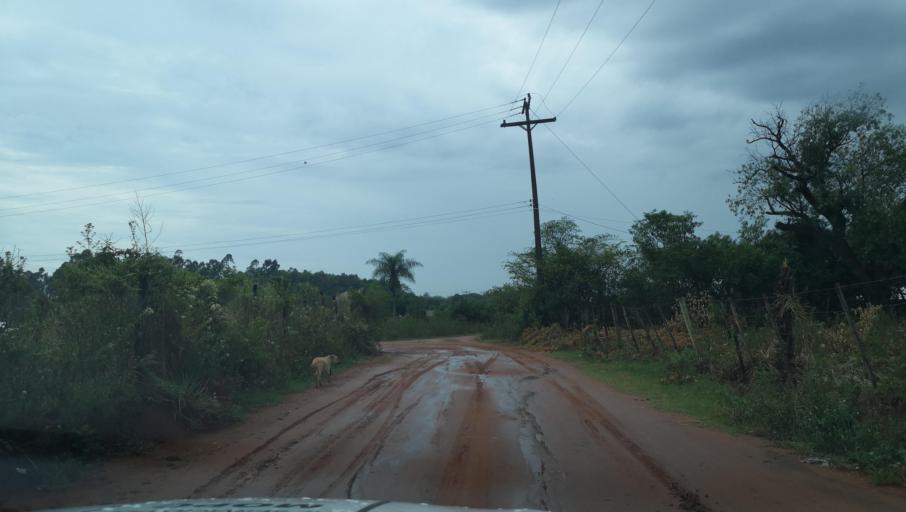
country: PY
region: Misiones
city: Santa Maria
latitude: -26.9015
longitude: -57.0340
